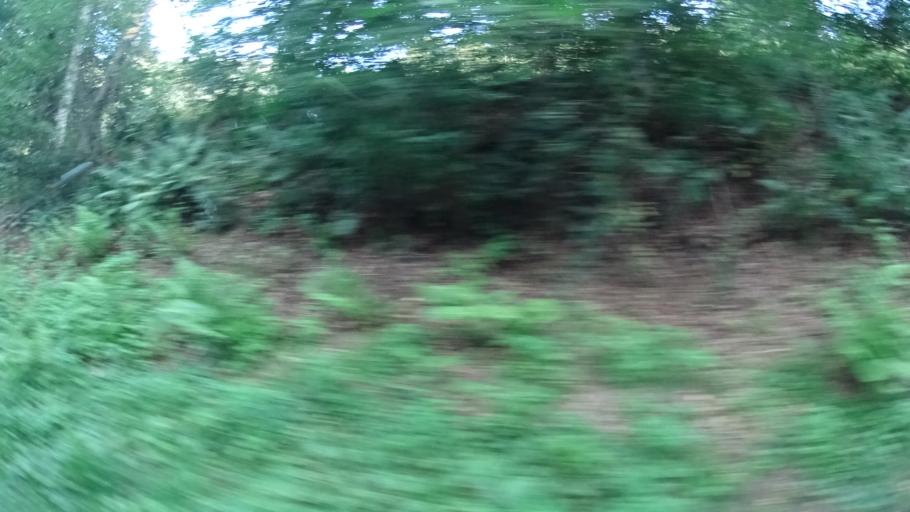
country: DE
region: Hesse
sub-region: Regierungsbezirk Darmstadt
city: Rothenberg
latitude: 49.5425
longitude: 8.9055
